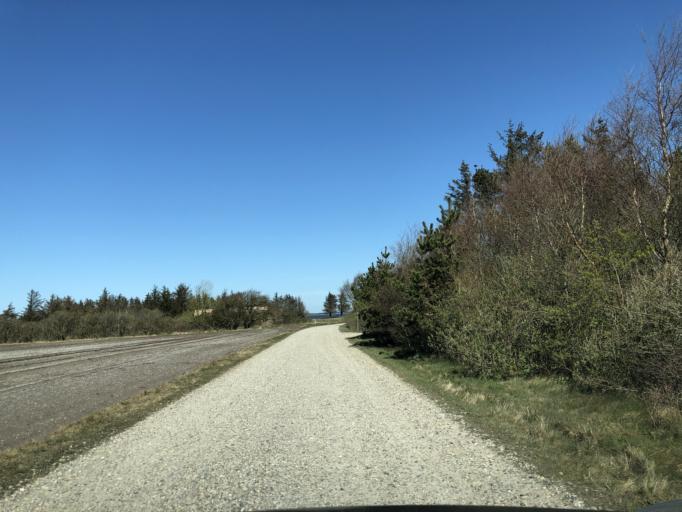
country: DK
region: Central Jutland
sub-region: Holstebro Kommune
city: Ulfborg
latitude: 56.3189
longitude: 8.1976
